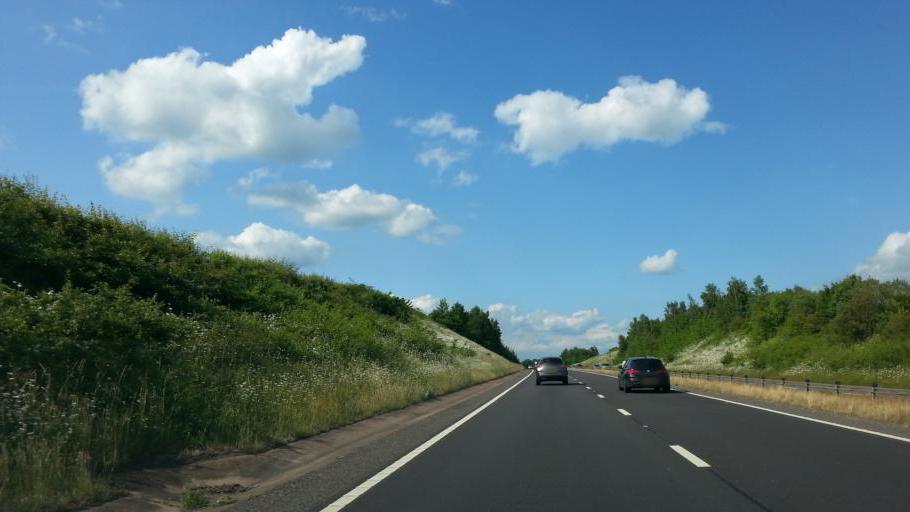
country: GB
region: England
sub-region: Warwickshire
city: Bidford-on-avon
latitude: 52.1801
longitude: -1.8791
